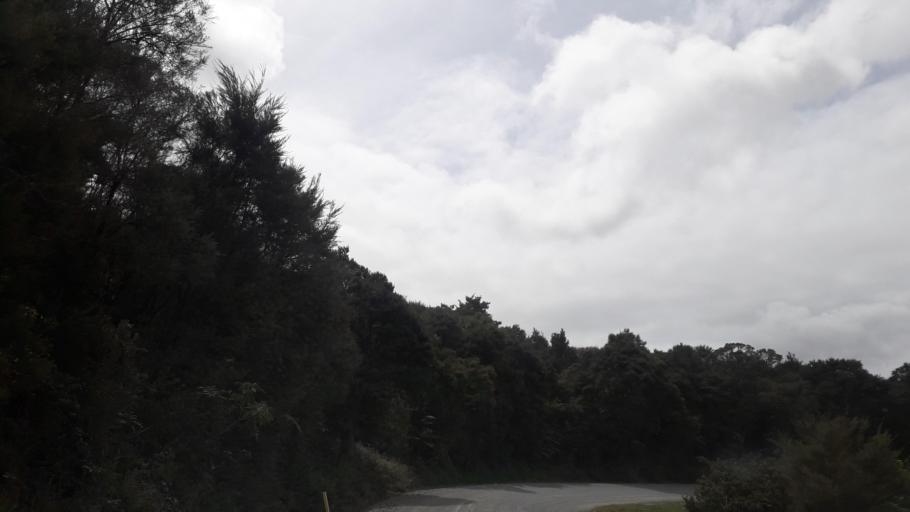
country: NZ
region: Northland
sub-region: Far North District
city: Taipa
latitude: -35.0364
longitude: 173.5647
